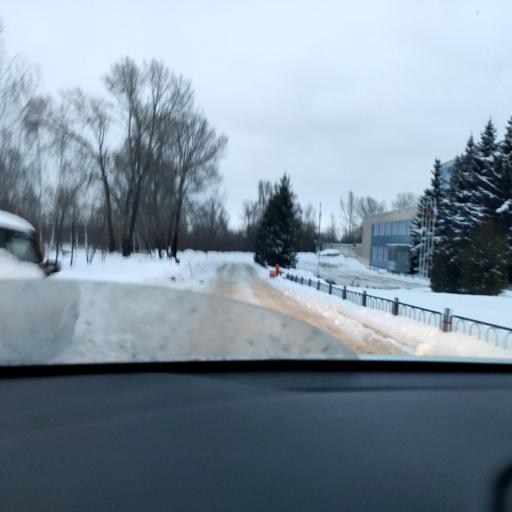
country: RU
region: Tatarstan
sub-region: Gorod Kazan'
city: Kazan
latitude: 55.8443
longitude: 49.0709
